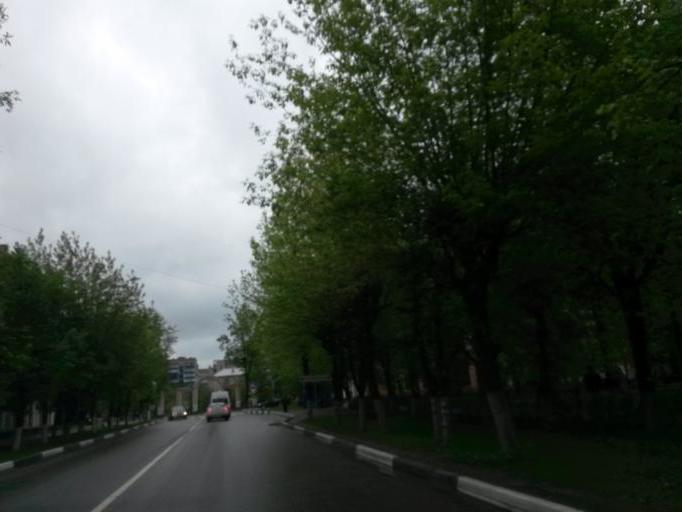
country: RU
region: Moskovskaya
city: Klimovsk
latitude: 55.3790
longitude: 37.5417
